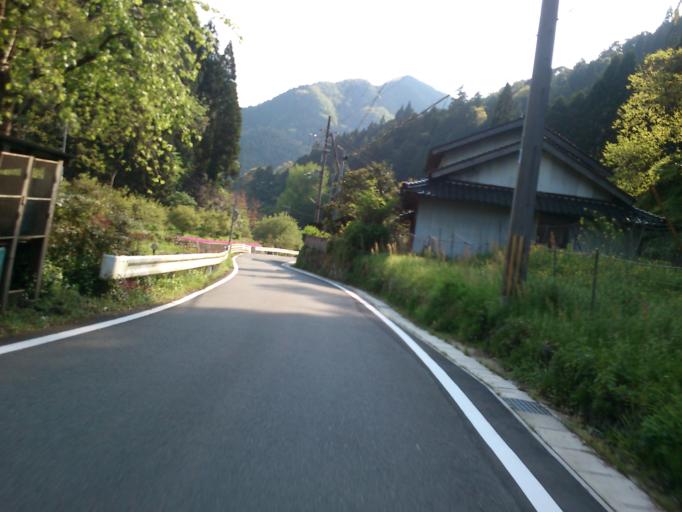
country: JP
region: Kyoto
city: Fukuchiyama
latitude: 35.3483
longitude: 135.0100
